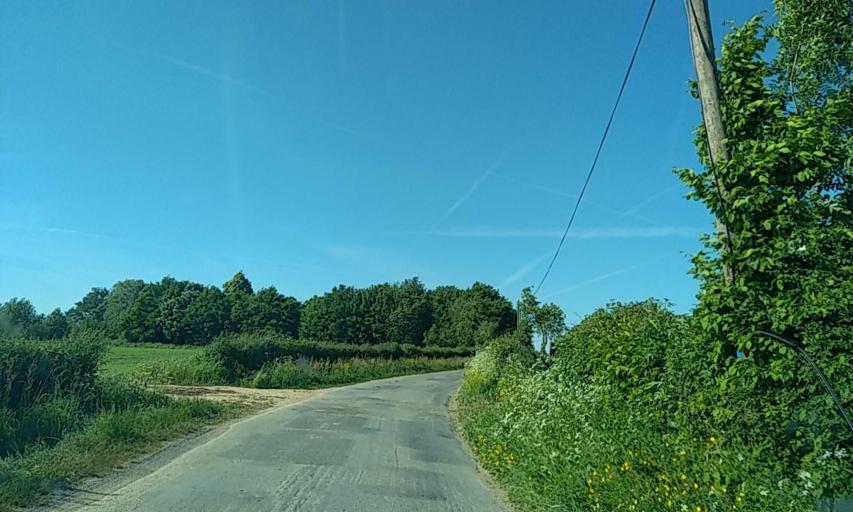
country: FR
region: Poitou-Charentes
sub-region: Departement des Deux-Sevres
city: Boisme
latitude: 46.7823
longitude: -0.4167
